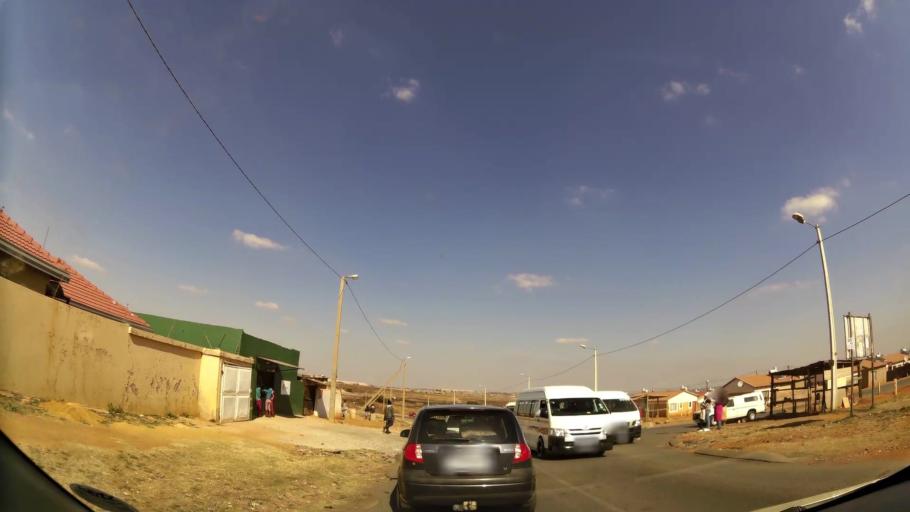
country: ZA
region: Gauteng
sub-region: West Rand District Municipality
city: Randfontein
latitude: -26.1714
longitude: 27.7777
